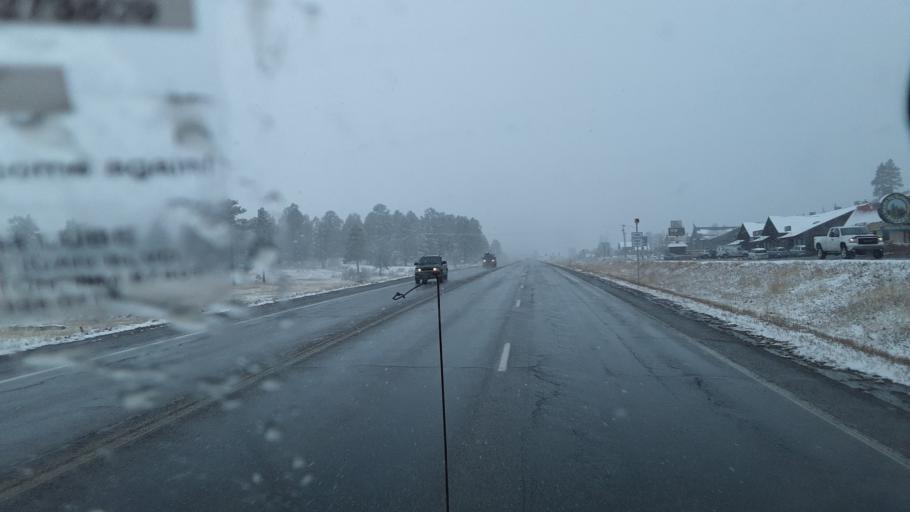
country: US
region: Colorado
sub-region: Archuleta County
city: Pagosa Springs
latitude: 37.2701
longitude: -107.0439
